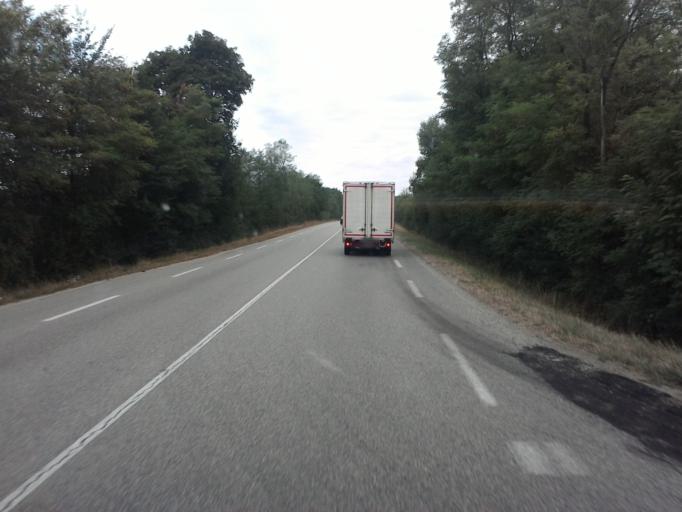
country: FR
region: Rhone-Alpes
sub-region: Departement de l'Ain
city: Ambronay
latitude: 46.0158
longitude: 5.3401
